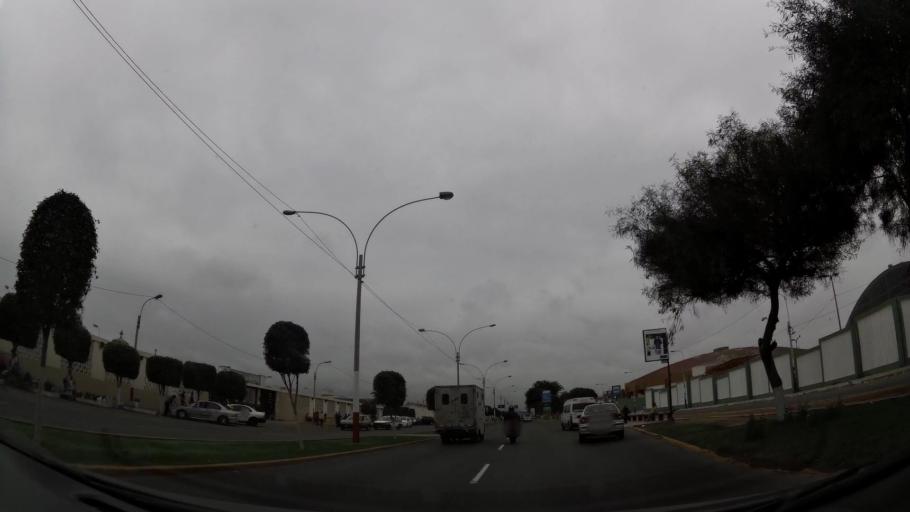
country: PE
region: Callao
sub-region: Callao
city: Callao
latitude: -12.0579
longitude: -77.1195
